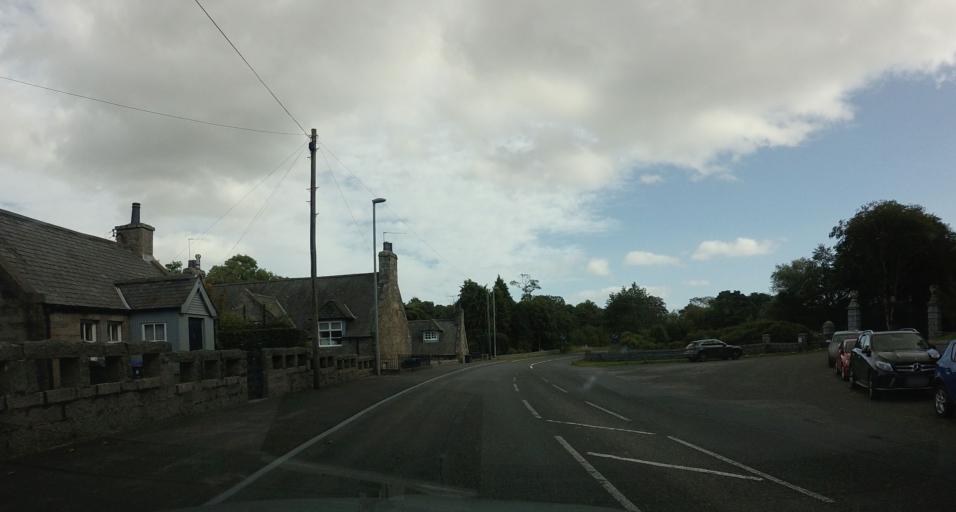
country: GB
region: Scotland
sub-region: Aberdeenshire
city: Kemnay
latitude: 57.1718
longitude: -2.4079
